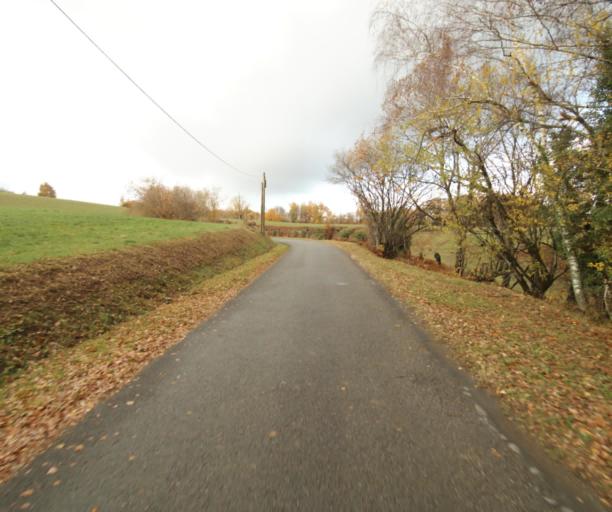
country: FR
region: Limousin
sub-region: Departement de la Correze
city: Sainte-Fereole
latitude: 45.2275
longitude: 1.6312
